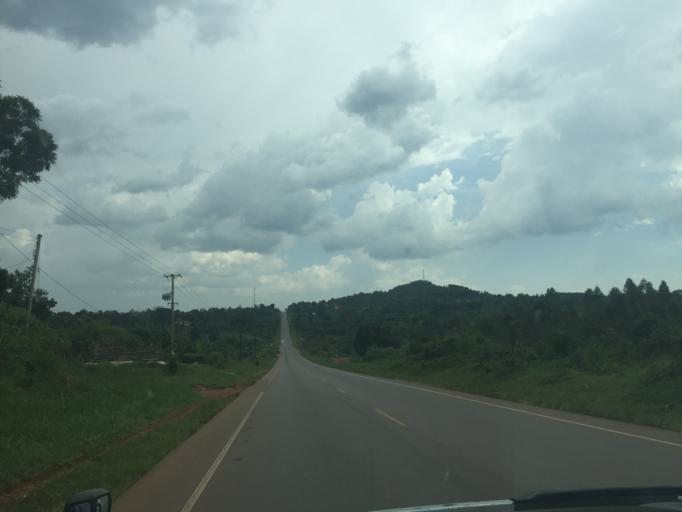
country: UG
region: Central Region
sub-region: Luwero District
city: Wobulenzi
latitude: 0.6587
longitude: 32.5301
